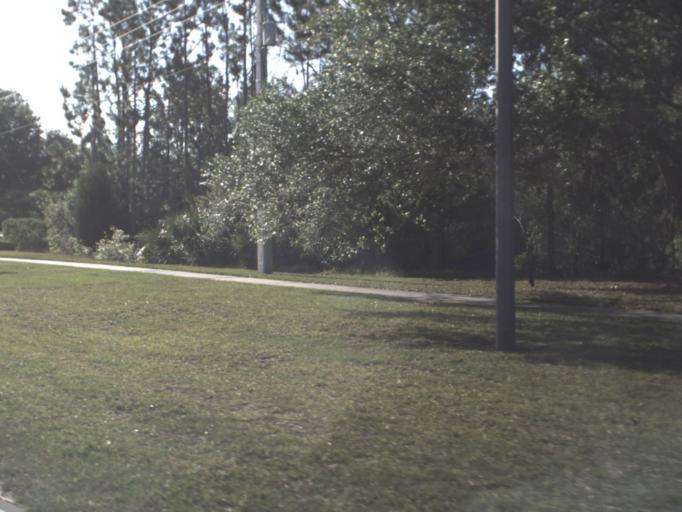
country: US
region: Florida
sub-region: Flagler County
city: Palm Coast
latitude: 29.5535
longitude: -81.2313
